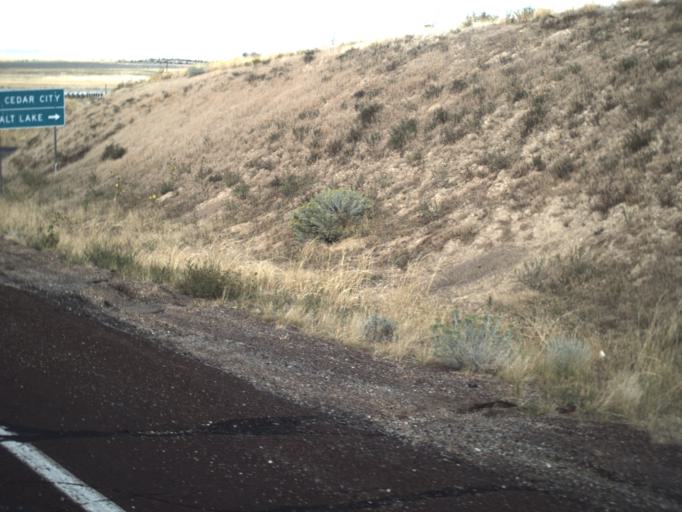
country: US
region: Utah
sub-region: Millard County
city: Fillmore
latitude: 38.7639
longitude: -112.5525
